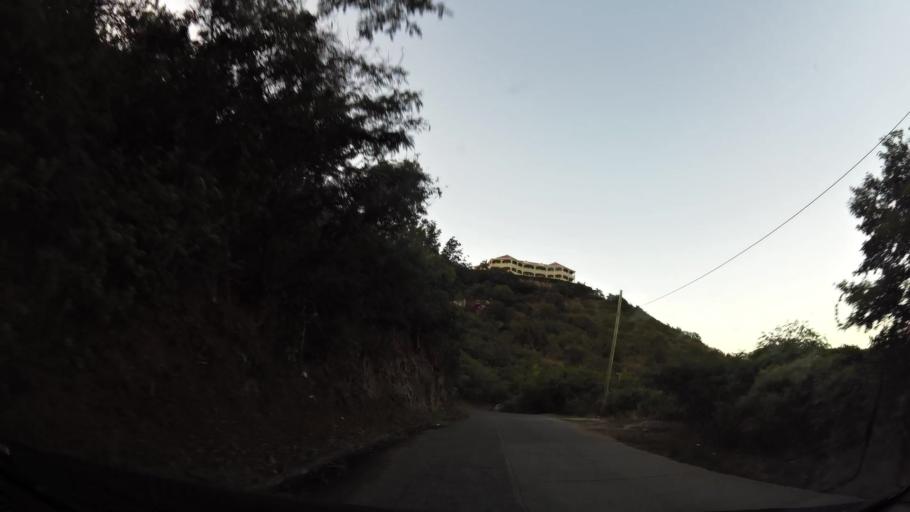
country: VG
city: Tortola
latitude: 18.4443
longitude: -64.5764
